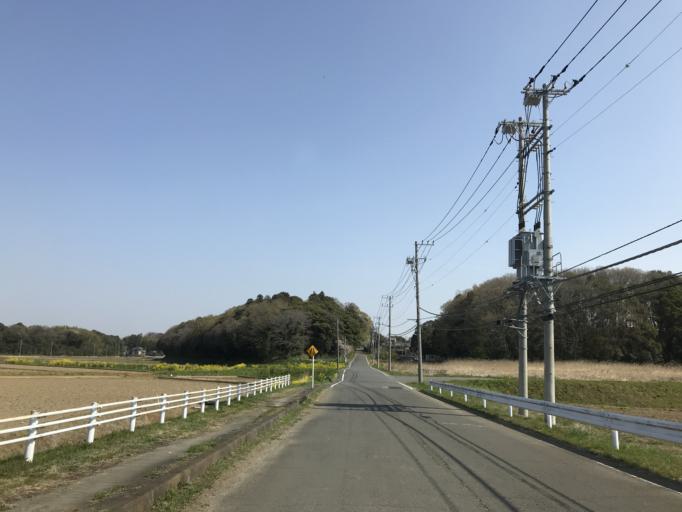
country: JP
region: Ibaraki
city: Moriya
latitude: 35.9403
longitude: 139.9597
